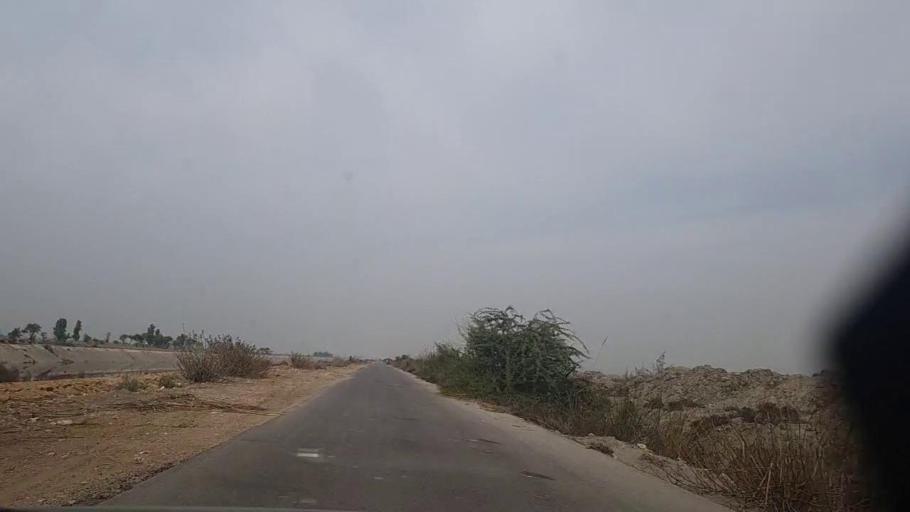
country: PK
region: Sindh
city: Sakrand
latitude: 26.2613
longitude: 68.2424
